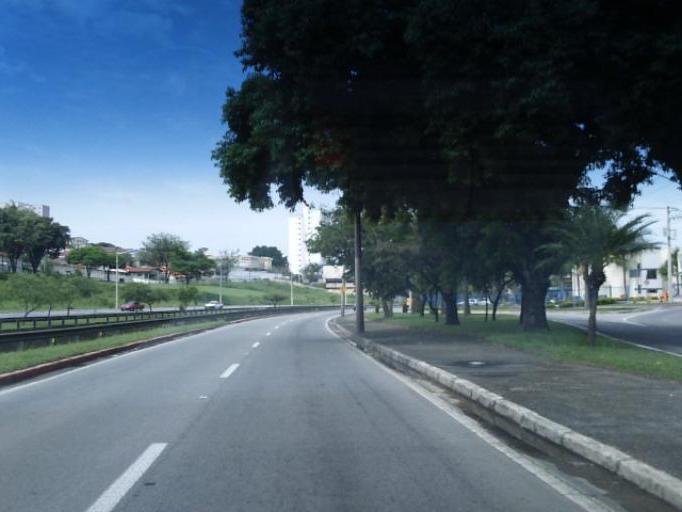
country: BR
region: Sao Paulo
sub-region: Sao Jose Dos Campos
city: Sao Jose dos Campos
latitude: -23.1852
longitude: -45.8779
